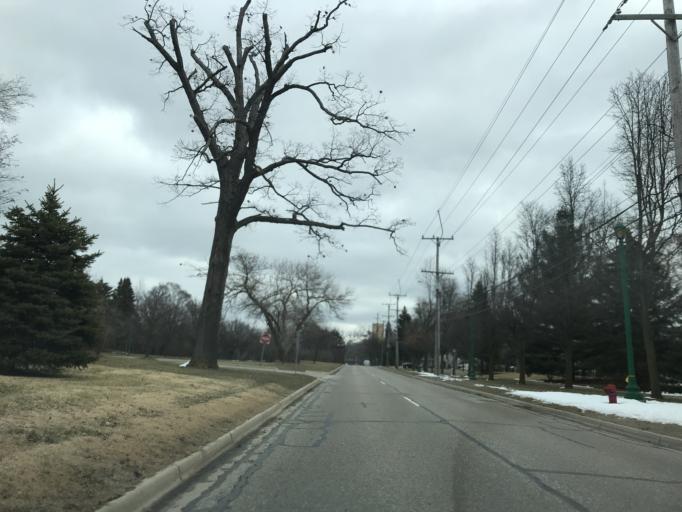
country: US
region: Michigan
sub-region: Oakland County
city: Bingham Farms
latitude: 42.4790
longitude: -83.2676
